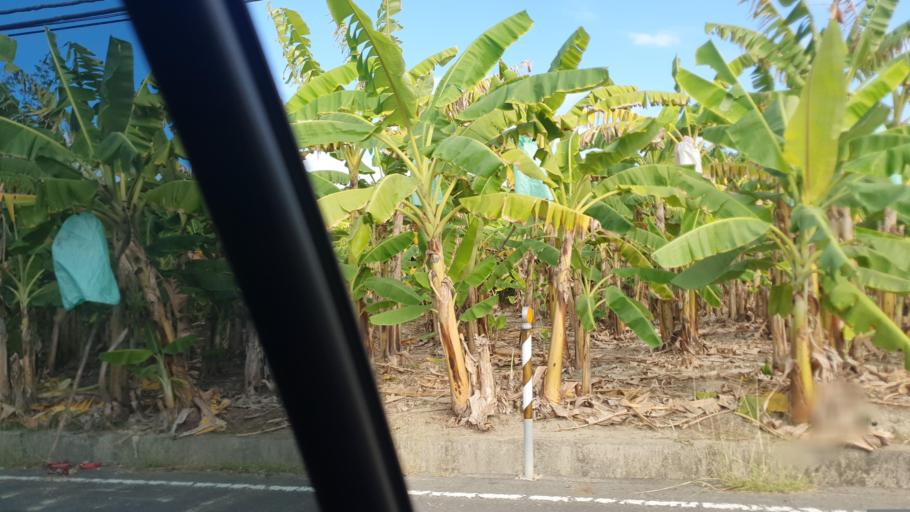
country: TW
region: Taiwan
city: Yujing
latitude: 23.0451
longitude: 120.4223
